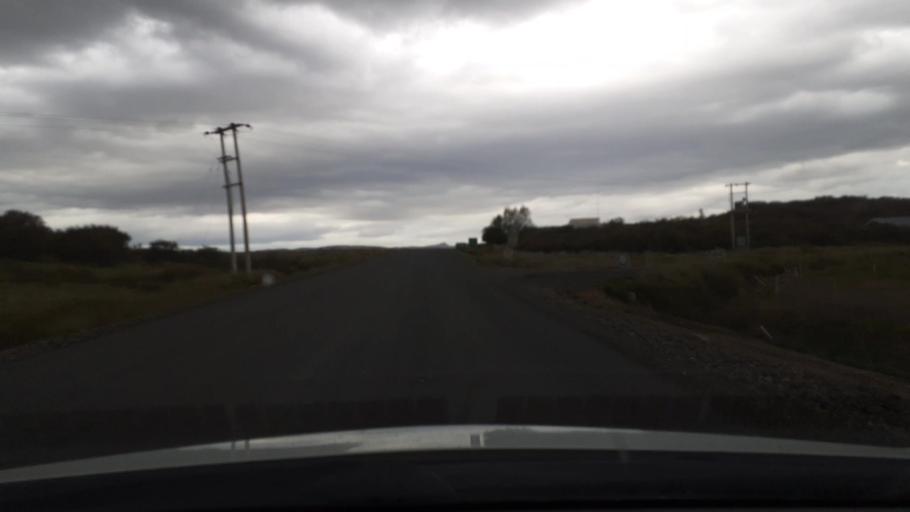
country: IS
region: West
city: Borgarnes
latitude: 64.6725
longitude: -21.7034
